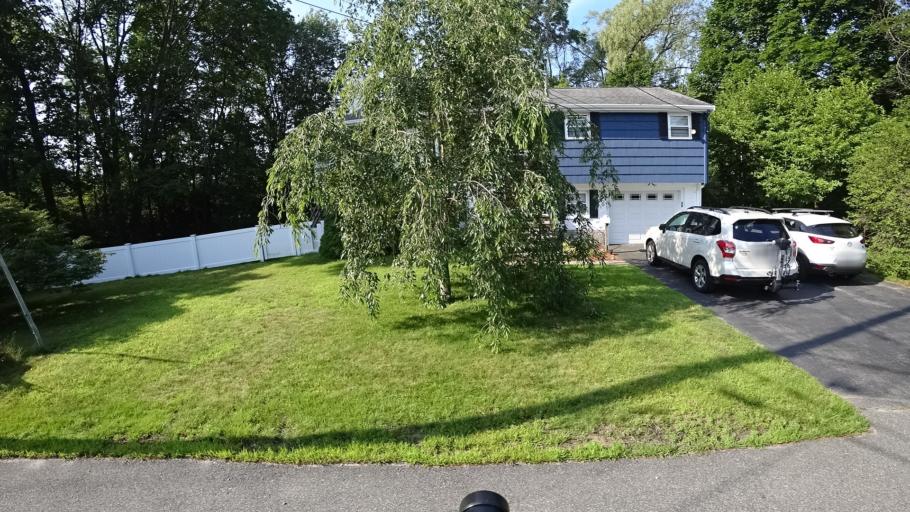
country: US
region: Massachusetts
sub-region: Norfolk County
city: Dedham
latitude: 42.2322
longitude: -71.1627
